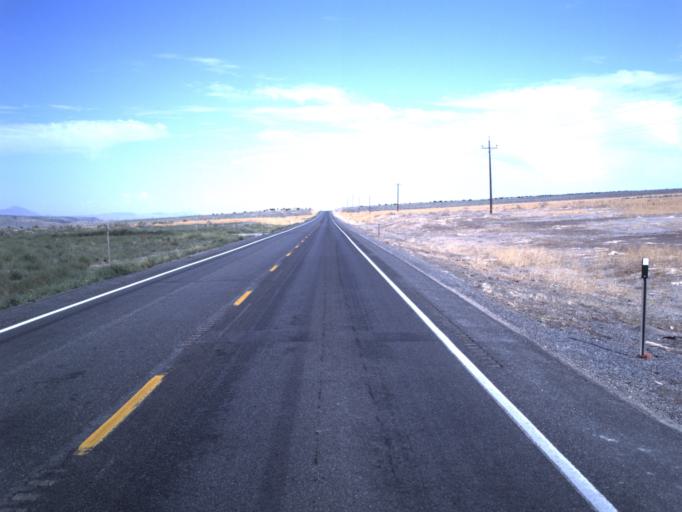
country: US
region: Utah
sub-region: Sanpete County
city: Gunnison
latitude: 39.2672
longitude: -111.8697
